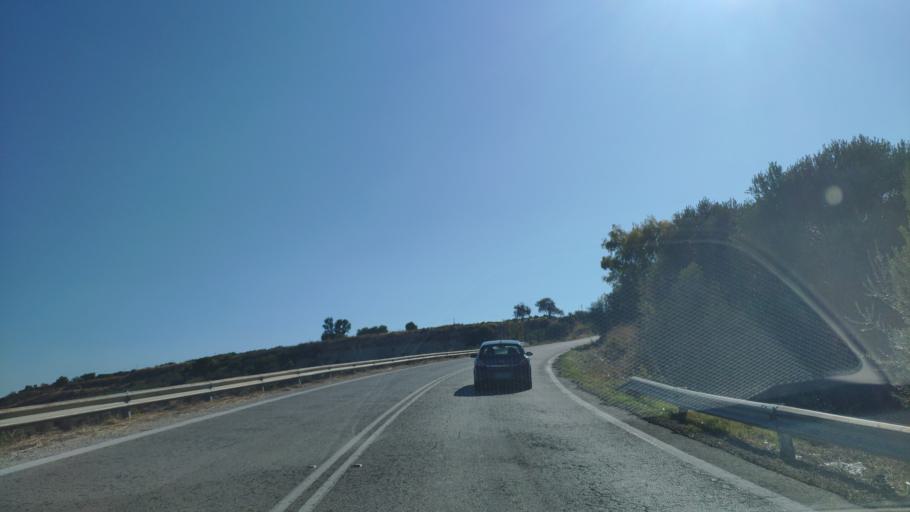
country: GR
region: Peloponnese
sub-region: Nomos Korinthias
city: Arkhaia Korinthos
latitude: 37.9155
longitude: 22.8946
